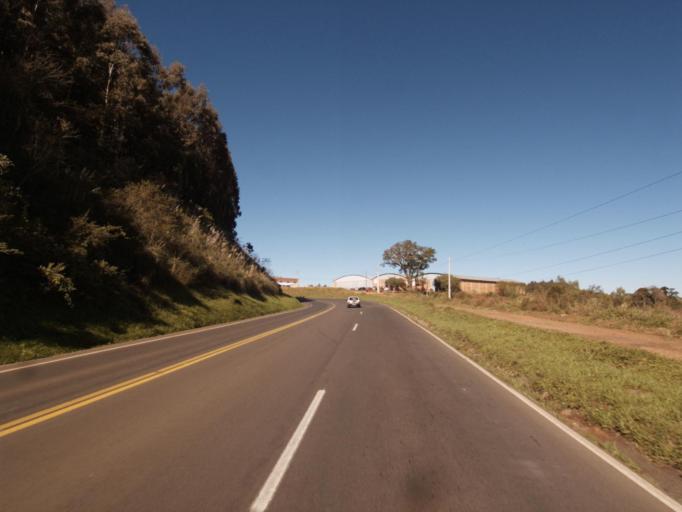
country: BR
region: Santa Catarina
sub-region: Chapeco
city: Chapeco
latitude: -26.9653
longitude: -52.5570
